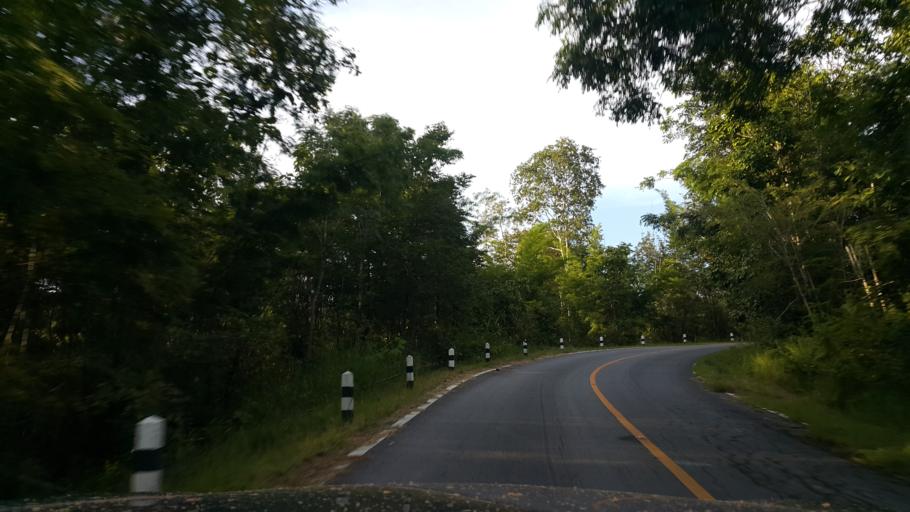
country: TH
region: Mae Hong Son
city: Mae Hi
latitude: 19.1816
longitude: 98.4102
